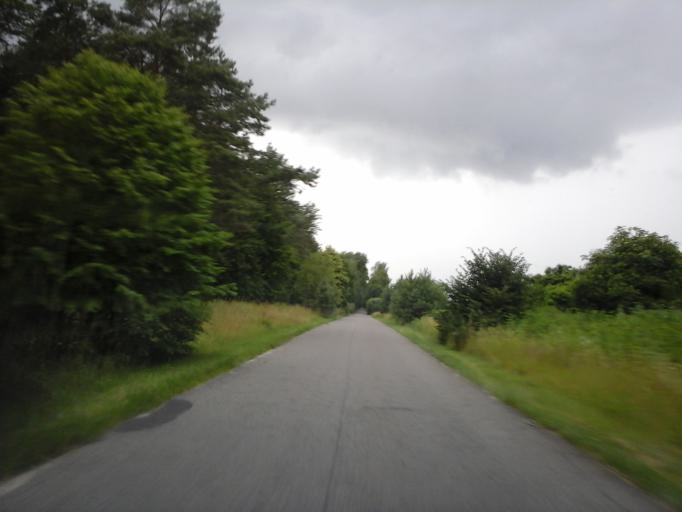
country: PL
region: West Pomeranian Voivodeship
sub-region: Powiat choszczenski
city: Bierzwnik
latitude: 53.0463
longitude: 15.6262
